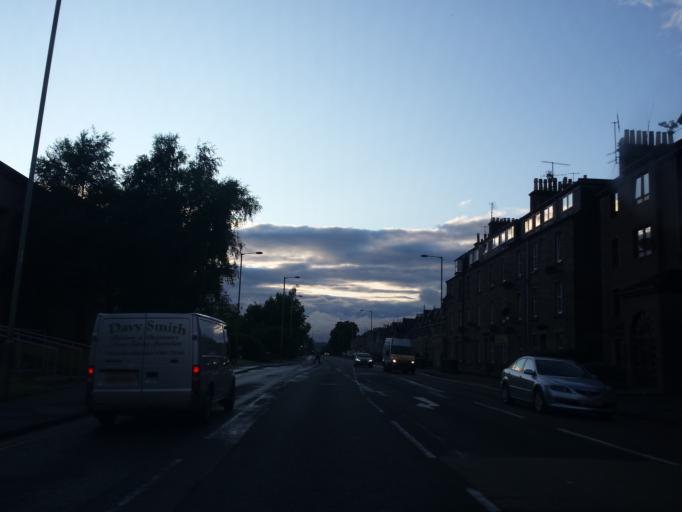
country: GB
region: Scotland
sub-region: Perth and Kinross
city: Perth
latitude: 56.4013
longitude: -3.4392
